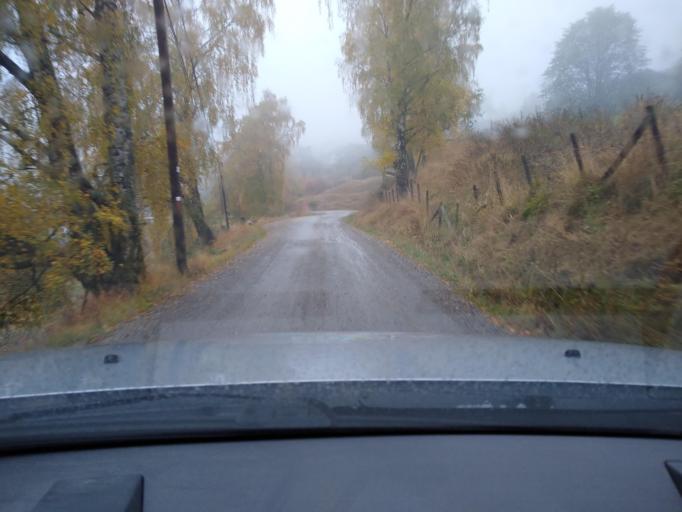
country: NO
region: Oppland
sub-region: Ringebu
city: Ringebu
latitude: 61.5304
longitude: 10.1514
